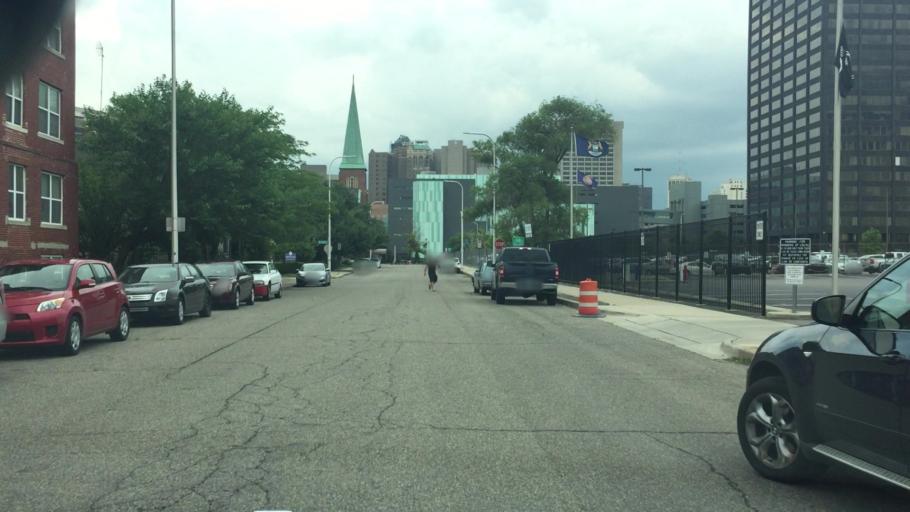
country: US
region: Michigan
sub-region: Wayne County
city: Detroit
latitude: 42.3286
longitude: -83.0625
